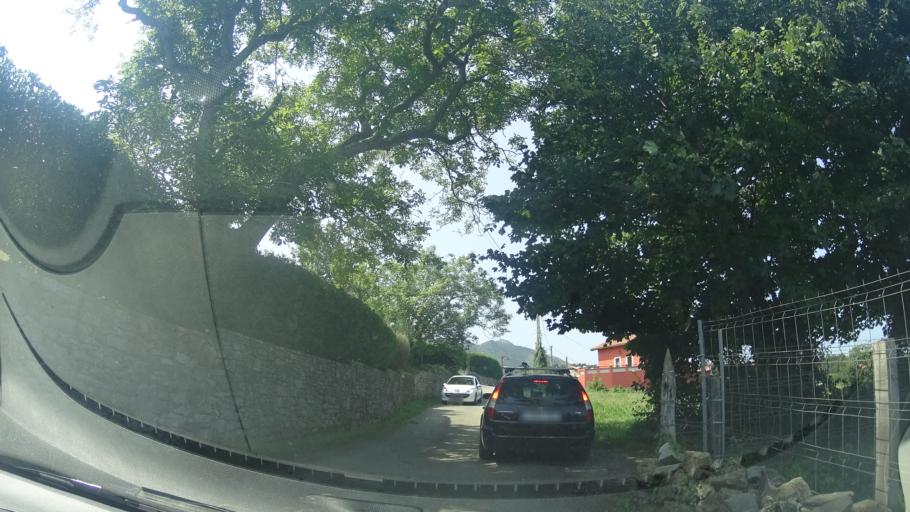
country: ES
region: Asturias
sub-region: Province of Asturias
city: Colunga
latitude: 43.4677
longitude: -5.2069
